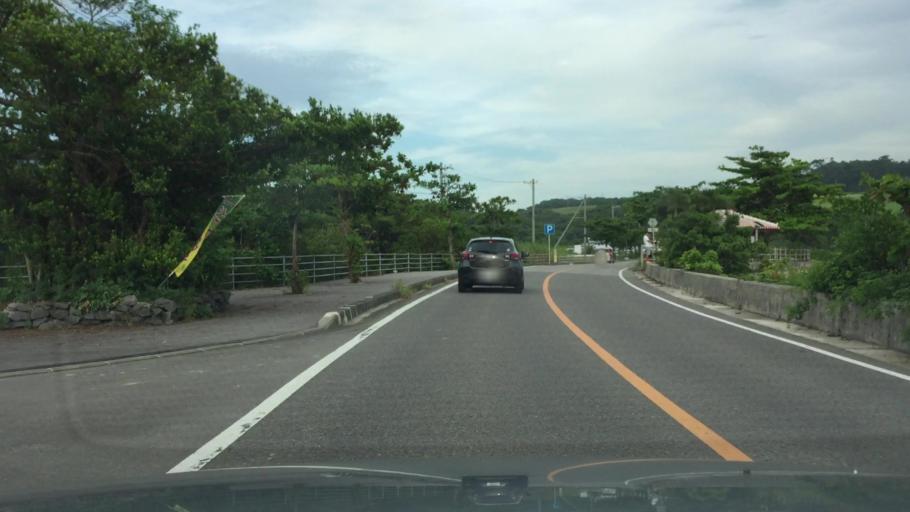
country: JP
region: Okinawa
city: Ishigaki
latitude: 24.4147
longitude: 124.1414
